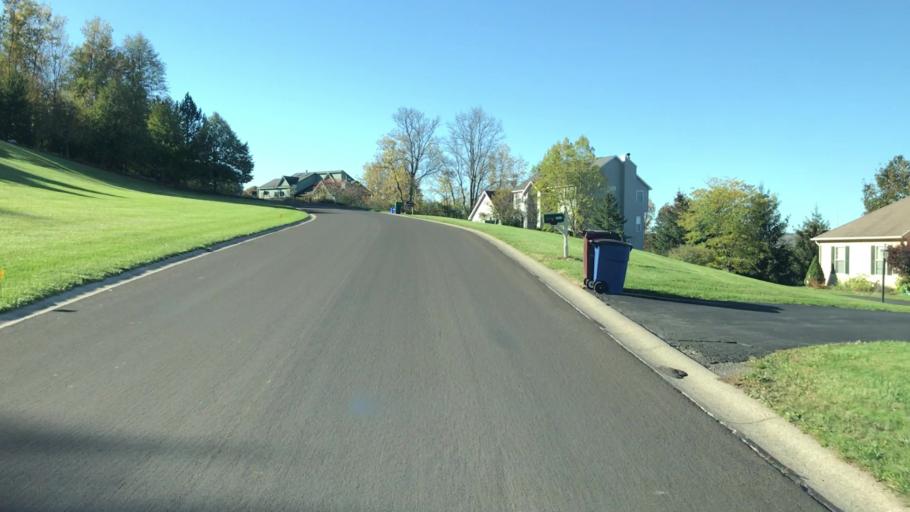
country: US
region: New York
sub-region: Onondaga County
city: Fayetteville
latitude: 42.9848
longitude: -76.0505
